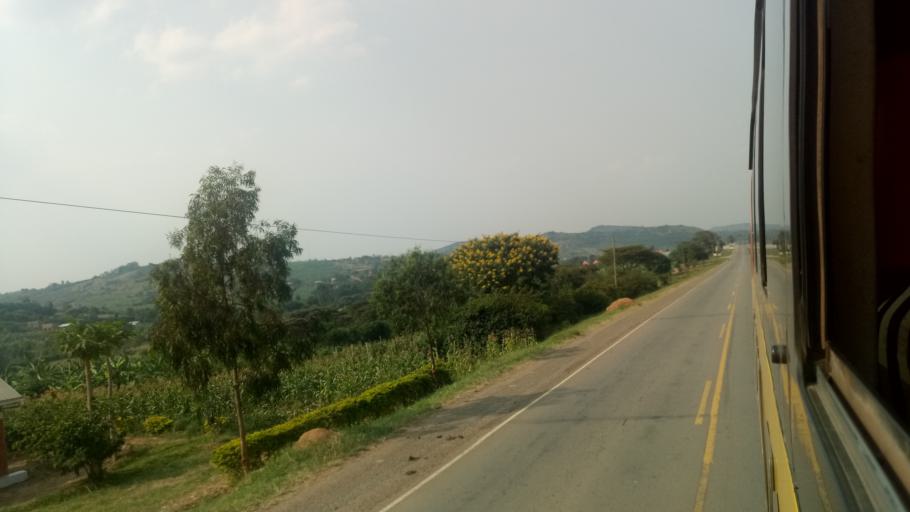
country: UG
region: Western Region
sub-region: Mbarara District
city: Mbarara
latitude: -0.5281
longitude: 30.7247
